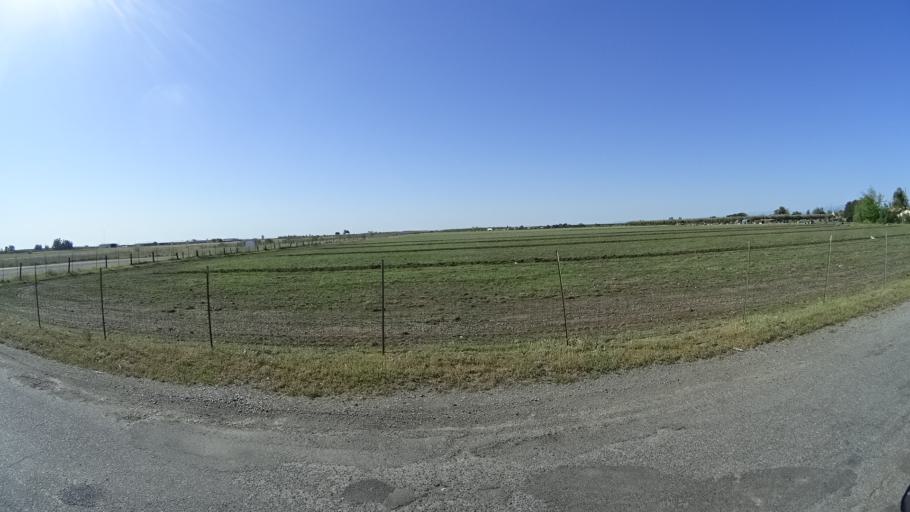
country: US
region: California
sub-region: Glenn County
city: Orland
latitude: 39.7290
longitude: -122.1505
